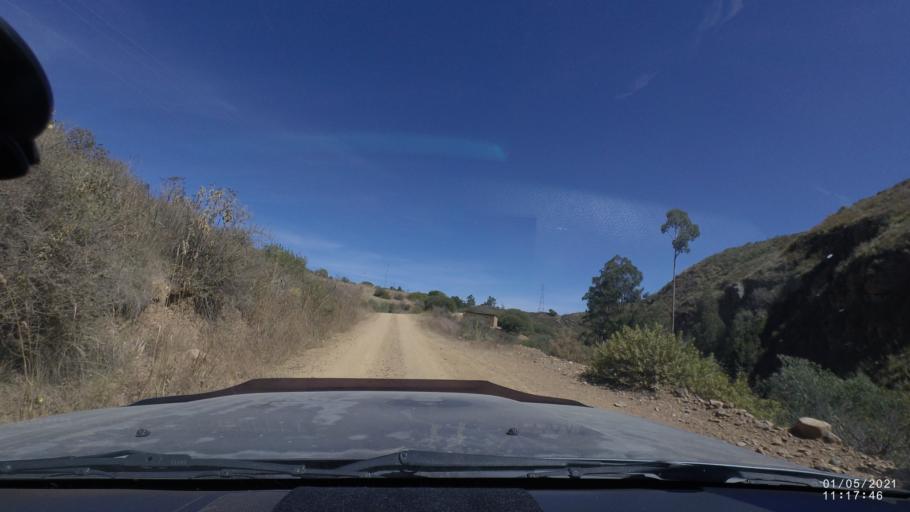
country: BO
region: Cochabamba
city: Tarata
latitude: -17.6400
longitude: -66.1151
